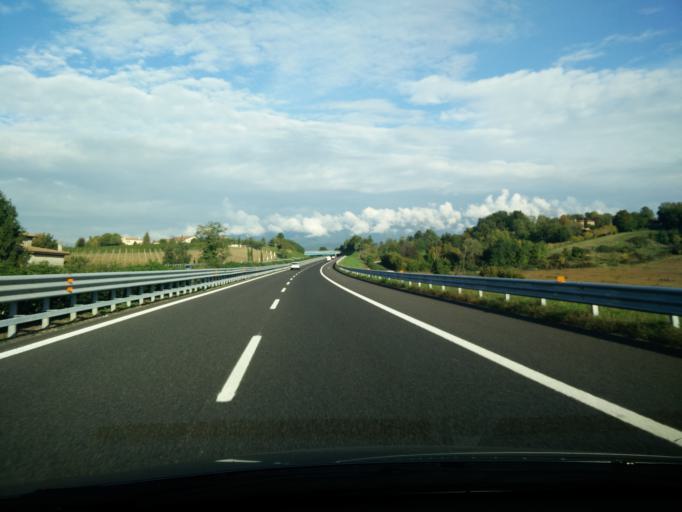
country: IT
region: Veneto
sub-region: Provincia di Treviso
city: San Martino
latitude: 45.9116
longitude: 12.3365
